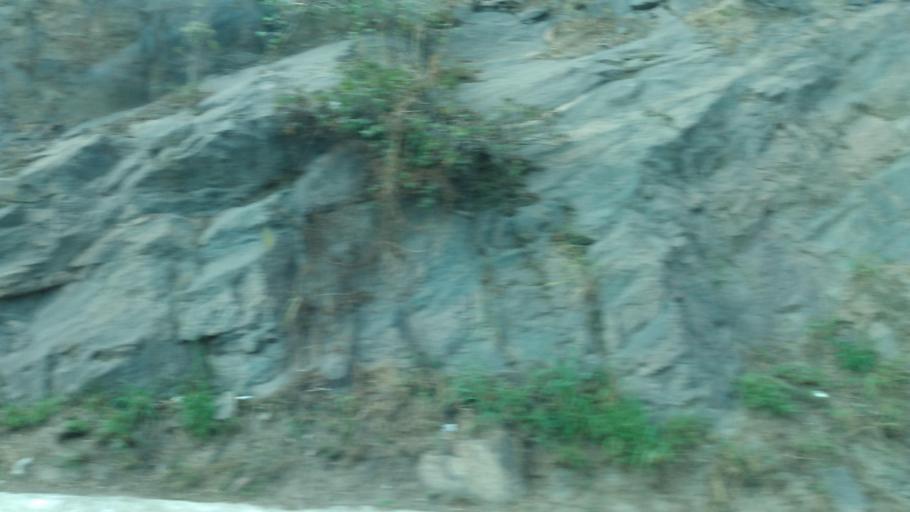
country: BR
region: Pernambuco
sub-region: Caruaru
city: Caruaru
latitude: -8.2998
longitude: -35.9928
